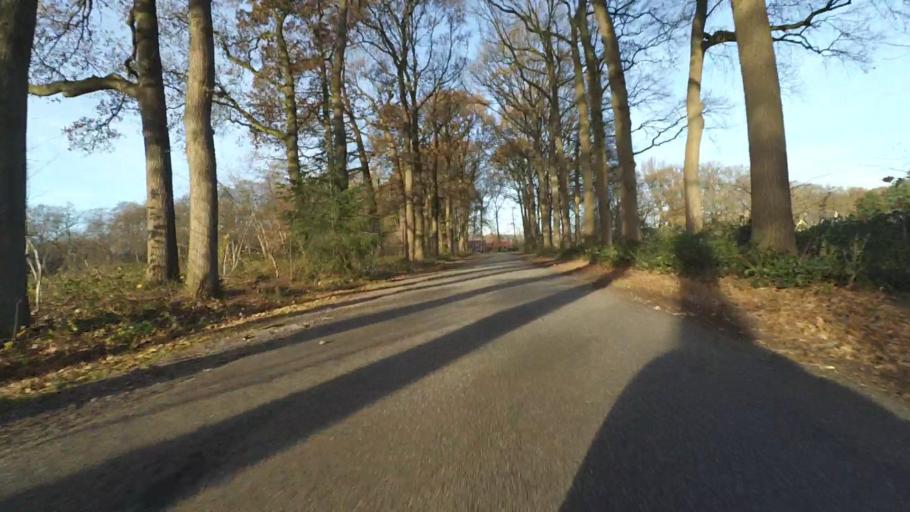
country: NL
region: Utrecht
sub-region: Gemeente Utrechtse Heuvelrug
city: Doorn
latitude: 52.0236
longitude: 5.3735
